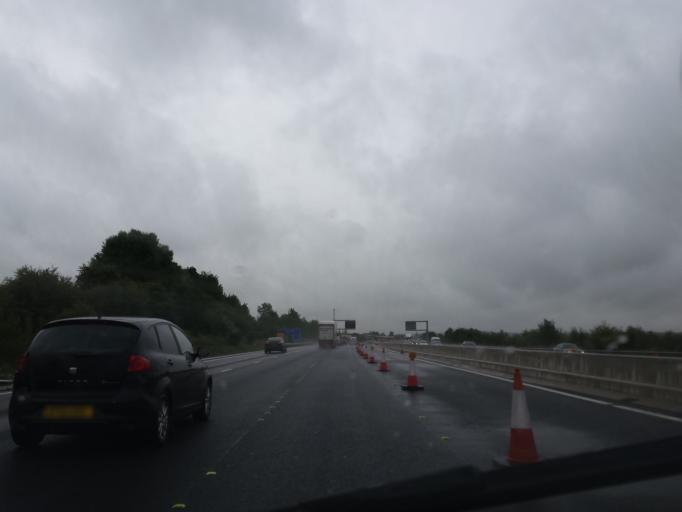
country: GB
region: England
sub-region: Rotherham
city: Wales
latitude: 53.3349
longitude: -1.2868
